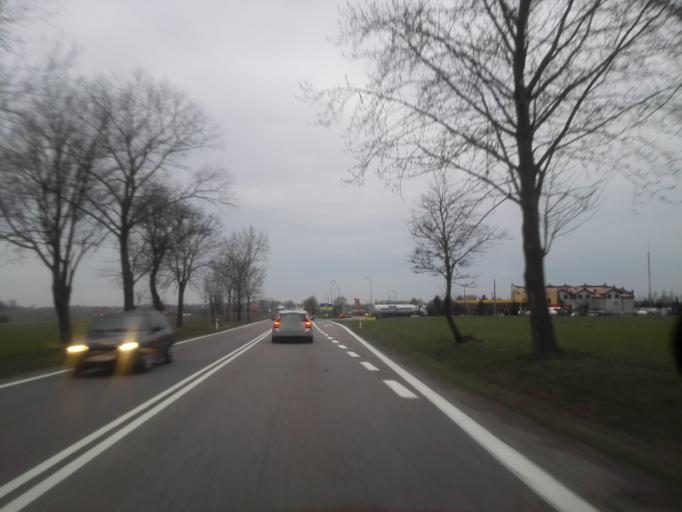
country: PL
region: Podlasie
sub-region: Powiat lomzynski
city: Piatnica
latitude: 53.2603
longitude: 22.1249
